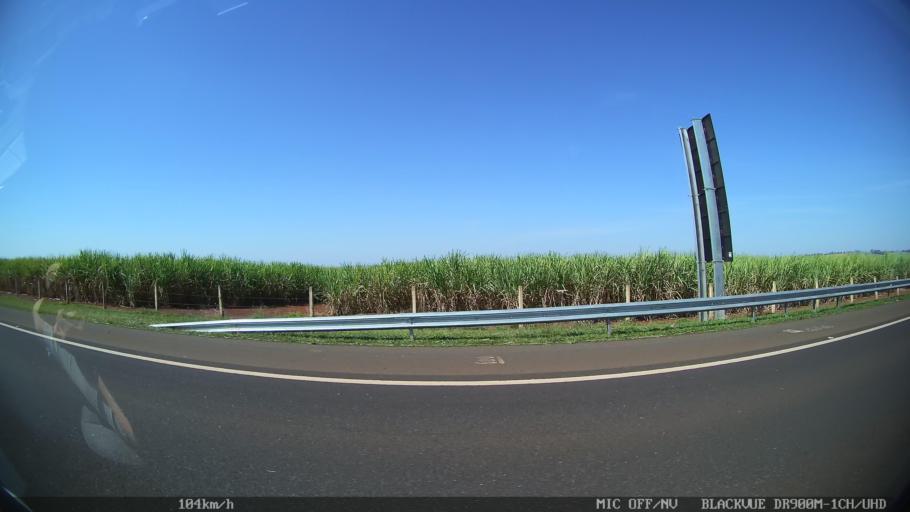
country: BR
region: Sao Paulo
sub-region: Batatais
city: Batatais
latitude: -20.7781
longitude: -47.5477
